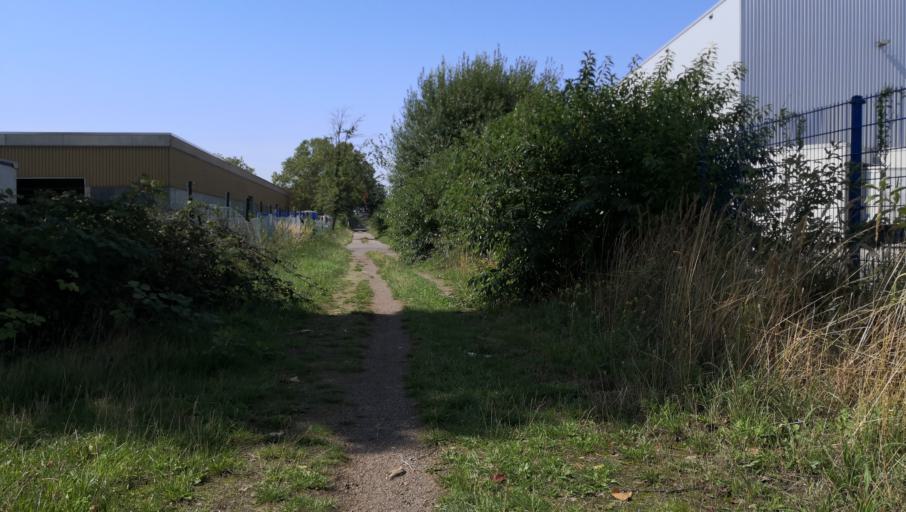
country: DE
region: North Rhine-Westphalia
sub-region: Regierungsbezirk Koln
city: Wahn-Heide
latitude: 50.8410
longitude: 7.1085
